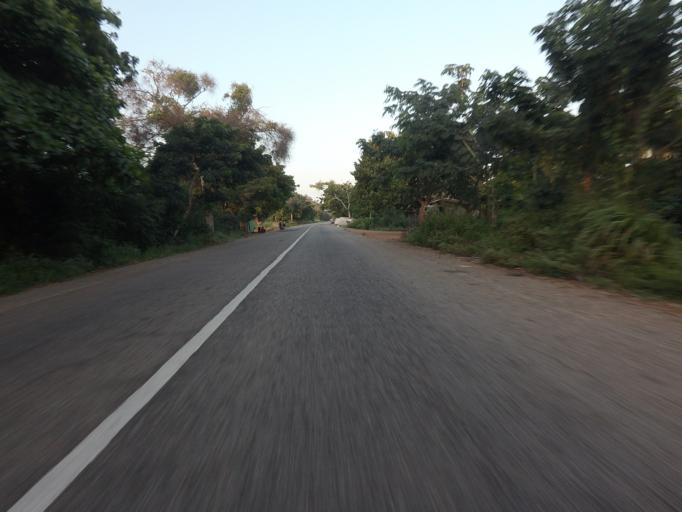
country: GH
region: Volta
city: Anloga
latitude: 5.7907
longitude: 0.8718
